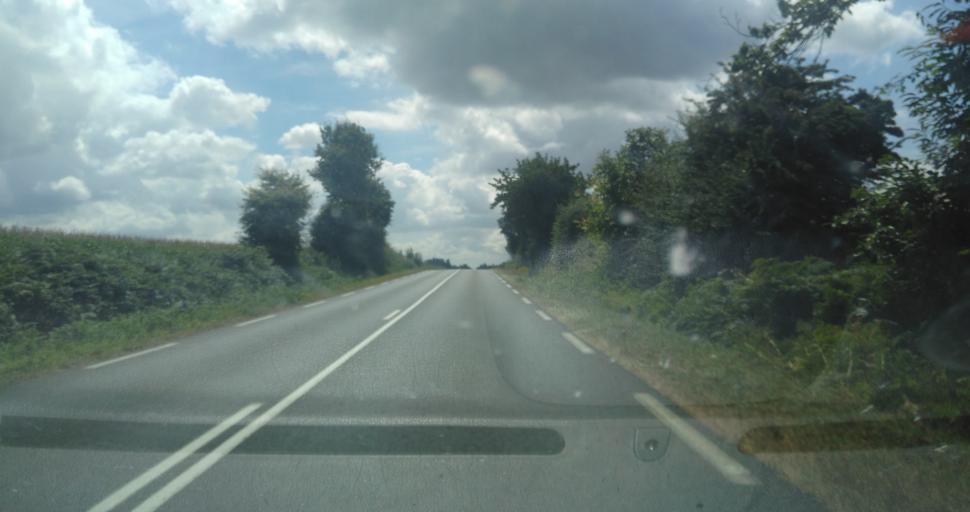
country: FR
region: Pays de la Loire
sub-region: Departement de la Vendee
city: Bournezeau
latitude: 46.6082
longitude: -1.1418
